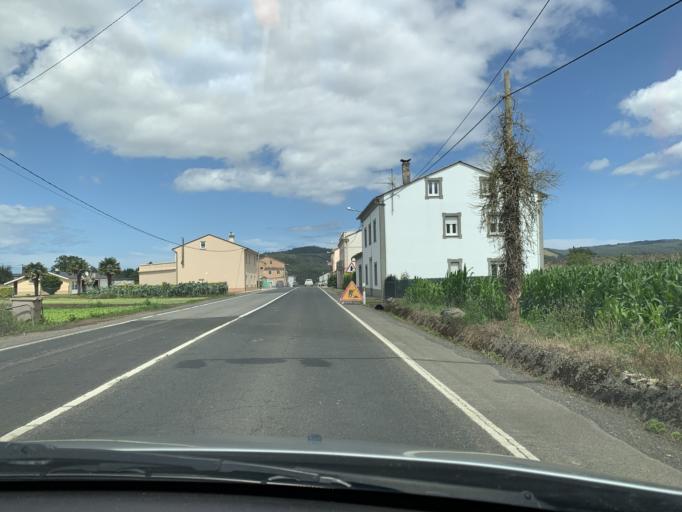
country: ES
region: Galicia
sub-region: Provincia de Lugo
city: Barreiros
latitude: 43.4951
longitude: -7.2745
